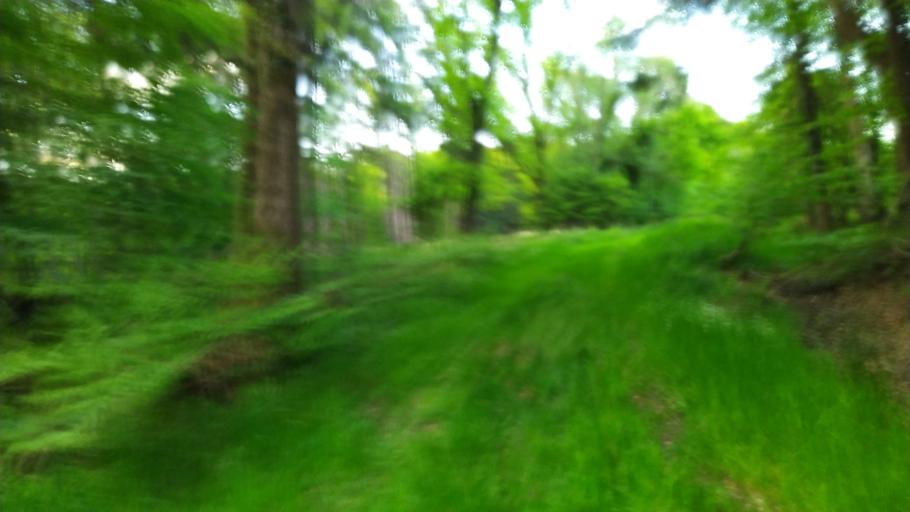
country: DE
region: Lower Saxony
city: Brest
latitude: 53.4350
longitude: 9.3728
